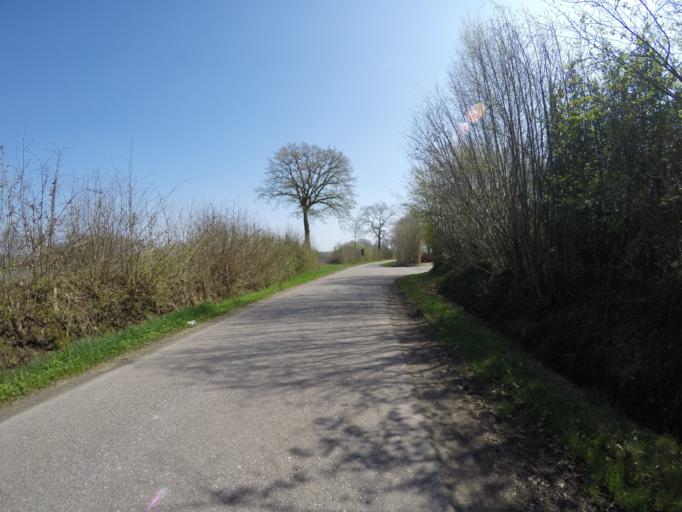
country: DE
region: Schleswig-Holstein
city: Hemdingen
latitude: 53.7585
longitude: 9.8520
